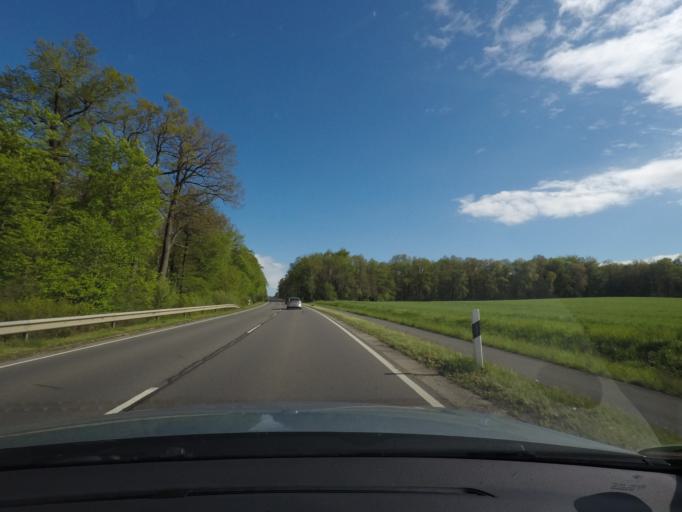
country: DE
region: Lower Saxony
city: Mariental
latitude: 52.2706
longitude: 10.9811
